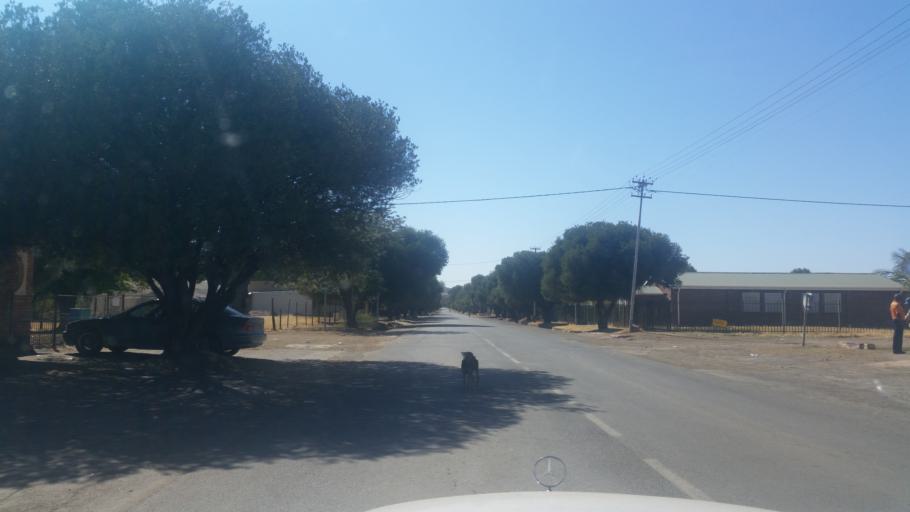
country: ZA
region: Orange Free State
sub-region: Xhariep District Municipality
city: Trompsburg
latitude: -30.4957
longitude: 25.9760
